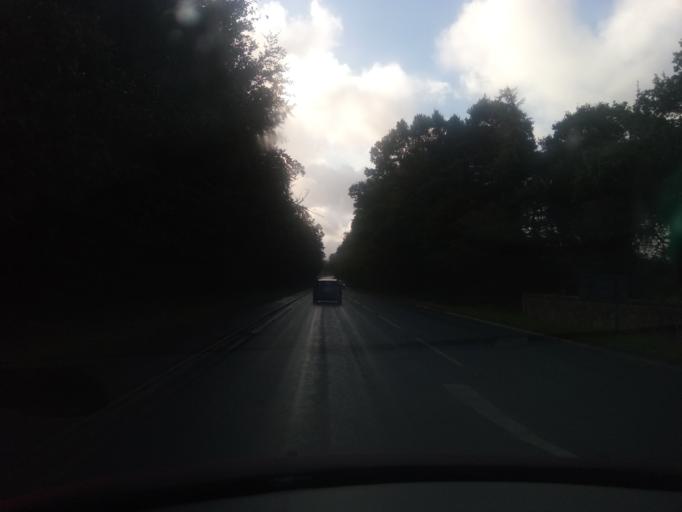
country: GB
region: England
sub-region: Cumbria
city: Carlisle
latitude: 54.9375
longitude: -2.9449
